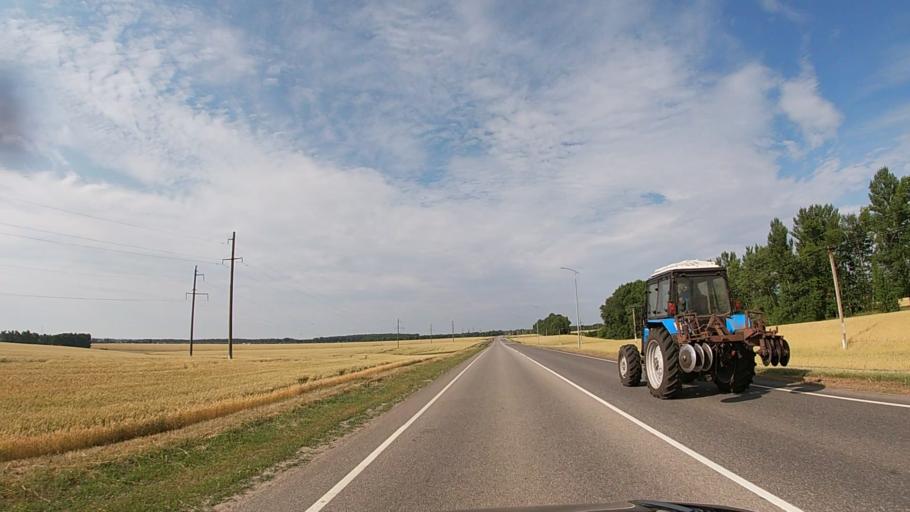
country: RU
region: Belgorod
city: Proletarskiy
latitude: 50.8131
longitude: 35.7495
